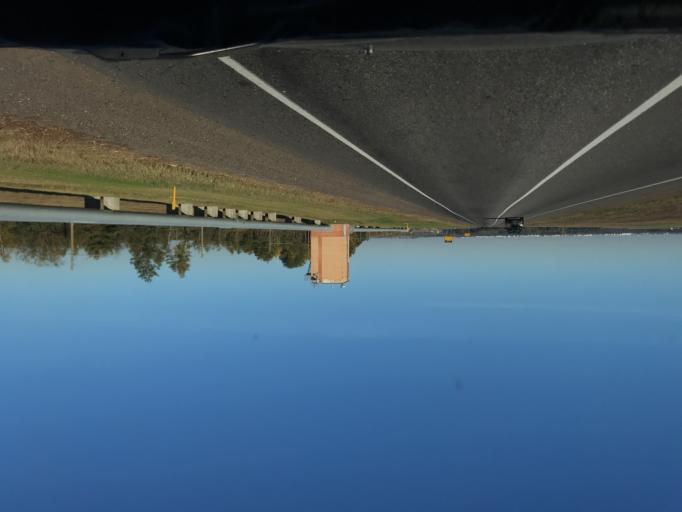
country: BY
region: Gomel
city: Mazyr
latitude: 51.9691
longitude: 29.2616
